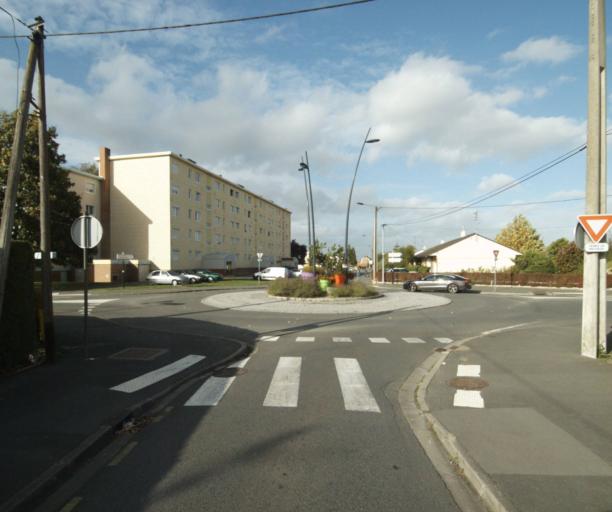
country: FR
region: Nord-Pas-de-Calais
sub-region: Departement du Nord
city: La Bassee
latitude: 50.5382
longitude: 2.8083
